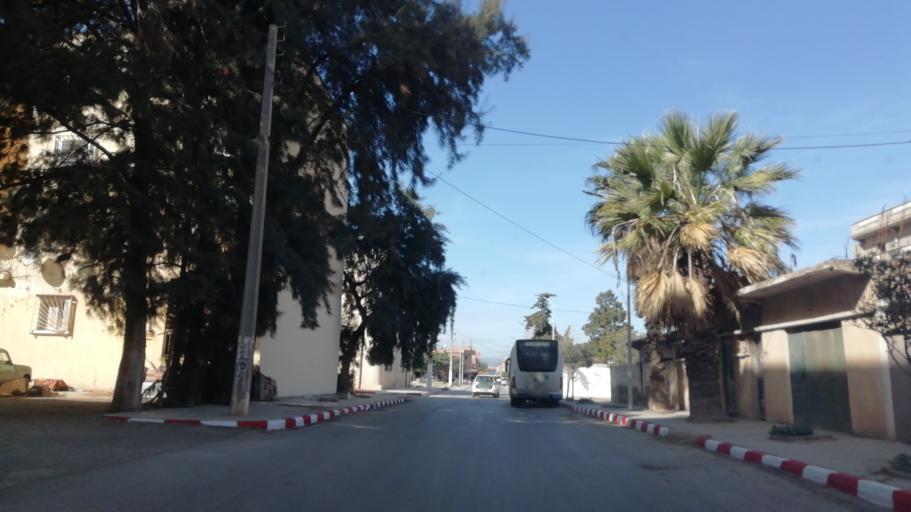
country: DZ
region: Oran
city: Es Senia
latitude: 35.6124
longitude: -0.5763
